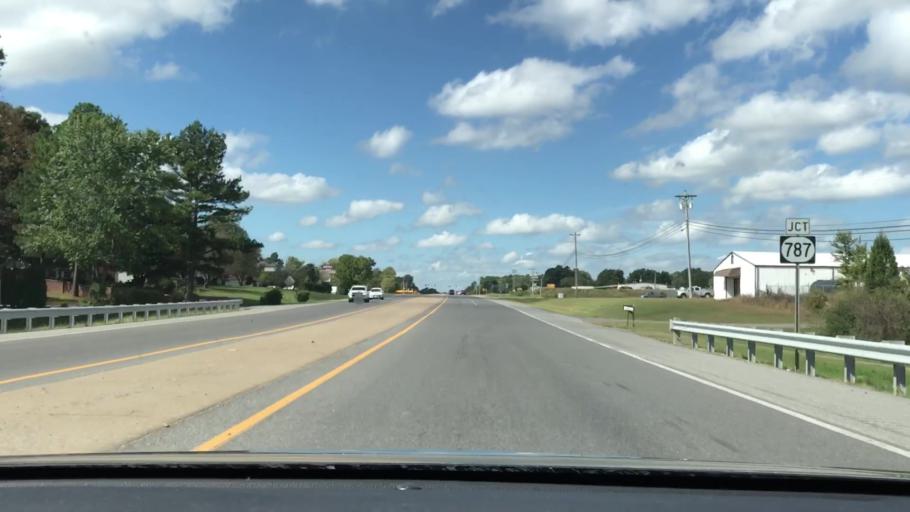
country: US
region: Kentucky
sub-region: McCracken County
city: Reidland
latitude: 37.0087
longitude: -88.5026
